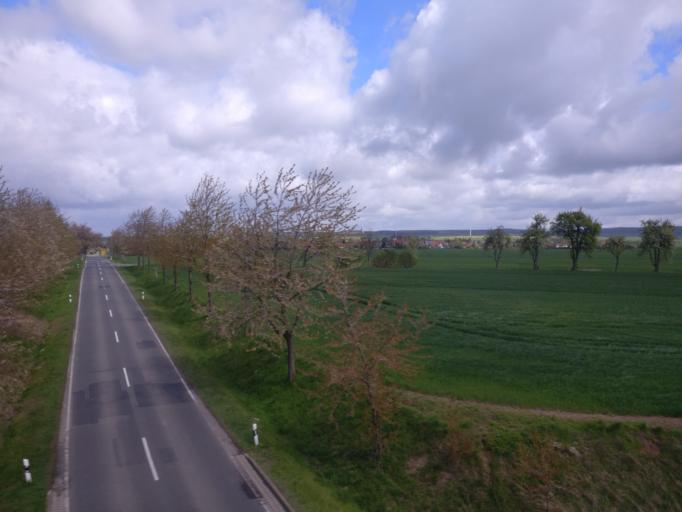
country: DE
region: Saxony-Anhalt
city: Derenburg
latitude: 51.9039
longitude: 10.8866
